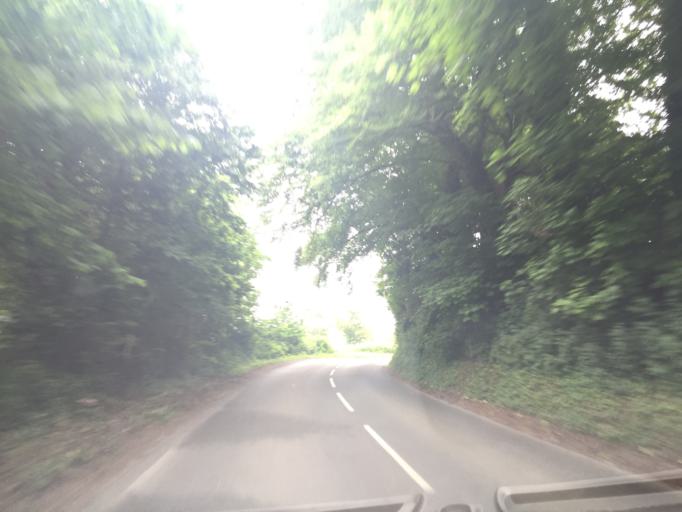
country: GB
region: England
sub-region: Dorset
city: Bovington Camp
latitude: 50.6583
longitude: -2.2755
